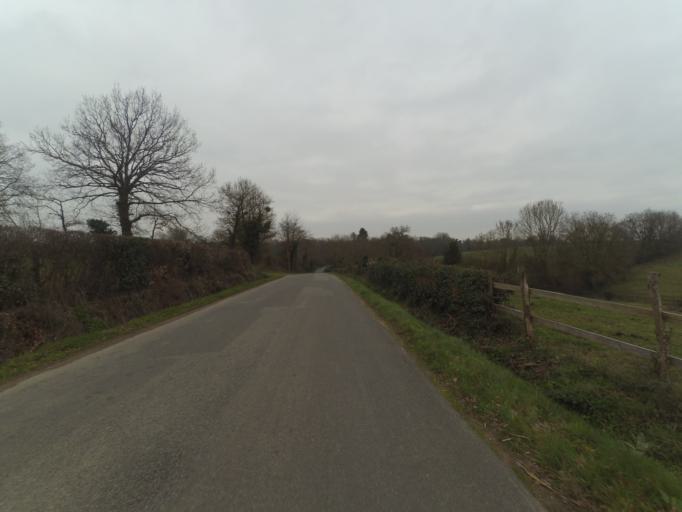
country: FR
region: Pays de la Loire
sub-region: Departement de la Loire-Atlantique
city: Coueron
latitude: 47.2342
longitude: -1.6963
